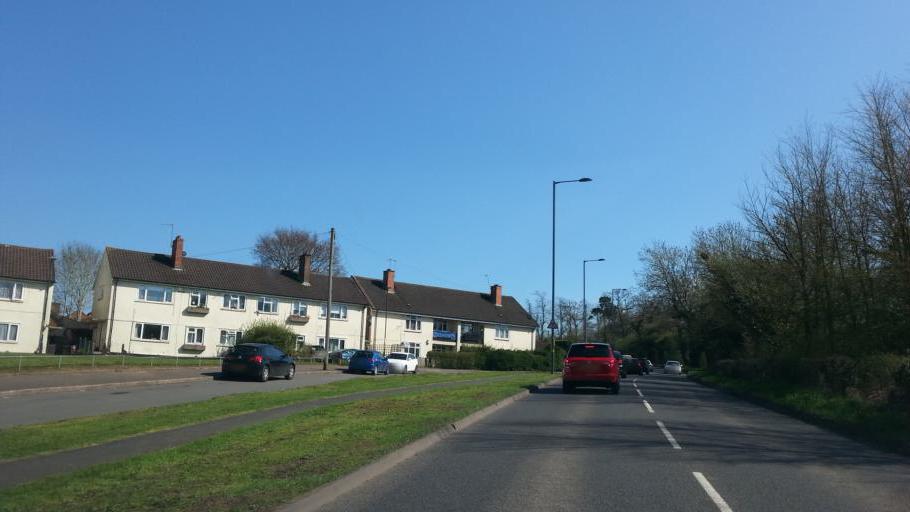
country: GB
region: England
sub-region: Worcestershire
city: Alvechurch
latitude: 52.3904
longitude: -1.9620
